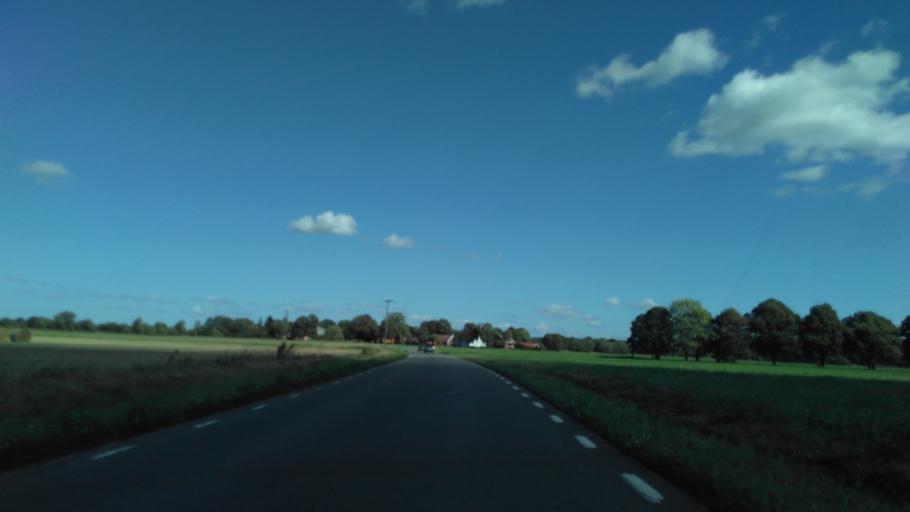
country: SE
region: Vaestra Goetaland
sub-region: Skara Kommun
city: Axvall
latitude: 58.4278
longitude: 13.6339
